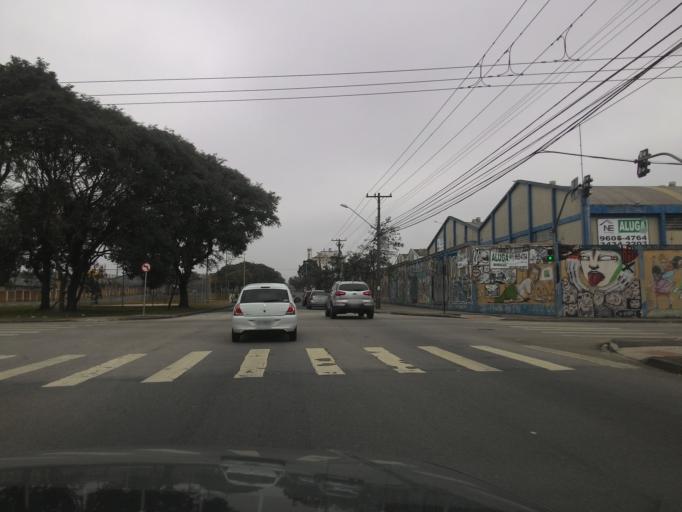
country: BR
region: Parana
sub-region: Curitiba
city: Curitiba
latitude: -25.4718
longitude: -49.2625
